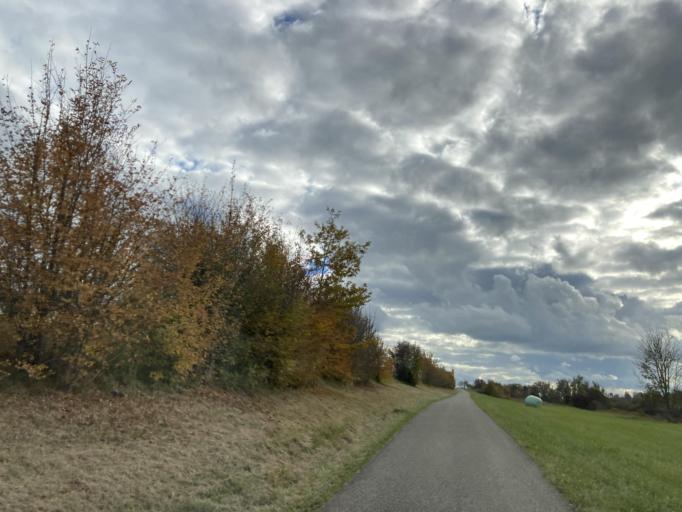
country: DE
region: Baden-Wuerttemberg
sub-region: Tuebingen Region
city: Dusslingen
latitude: 48.4677
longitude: 9.0634
